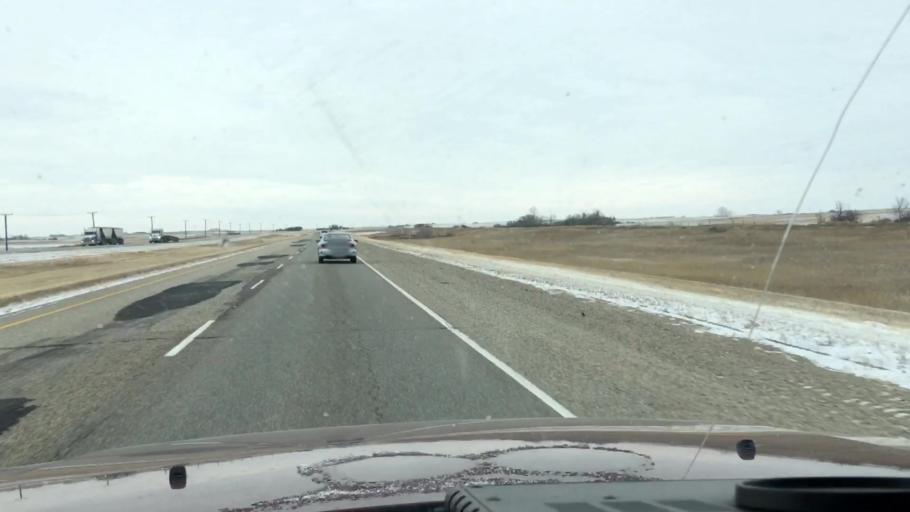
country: CA
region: Saskatchewan
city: Watrous
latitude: 51.4432
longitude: -106.2120
